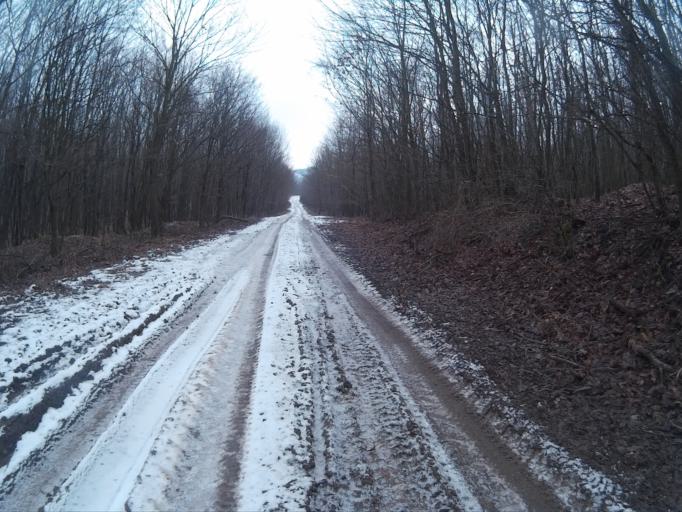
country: HU
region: Komarom-Esztergom
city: Tarjan
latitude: 47.5845
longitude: 18.5252
